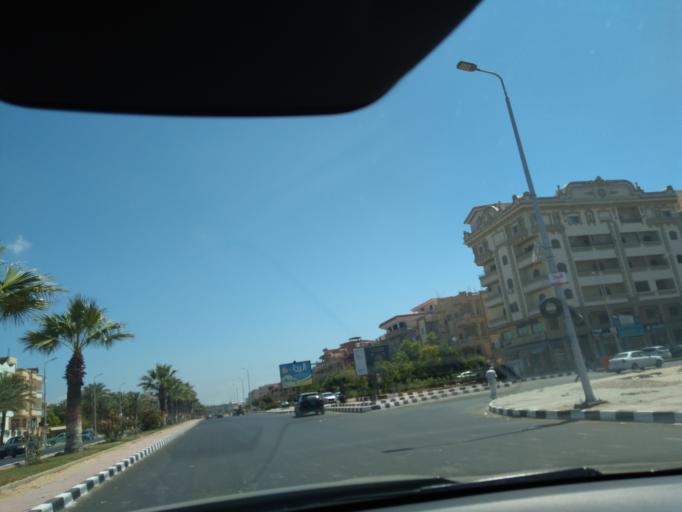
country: EG
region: Dumyat
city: Faraskur
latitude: 31.4299
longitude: 31.6738
